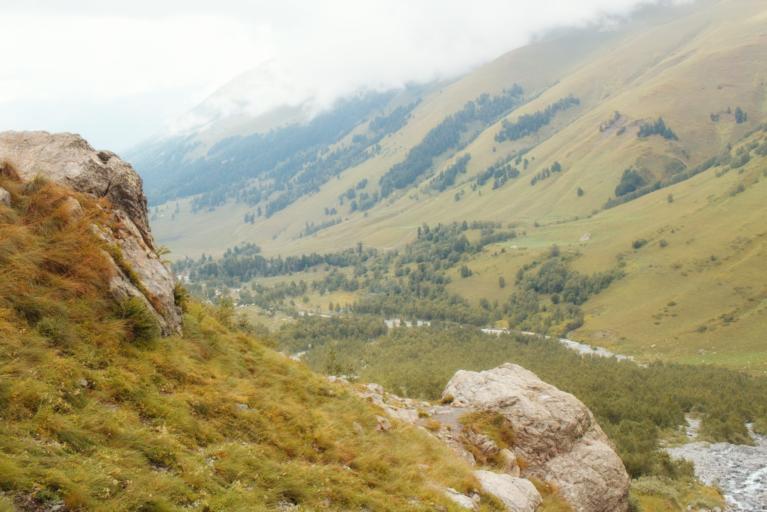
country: RU
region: Karachayevo-Cherkesiya
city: Nizhniy Arkhyz
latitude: 43.4375
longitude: 41.2797
